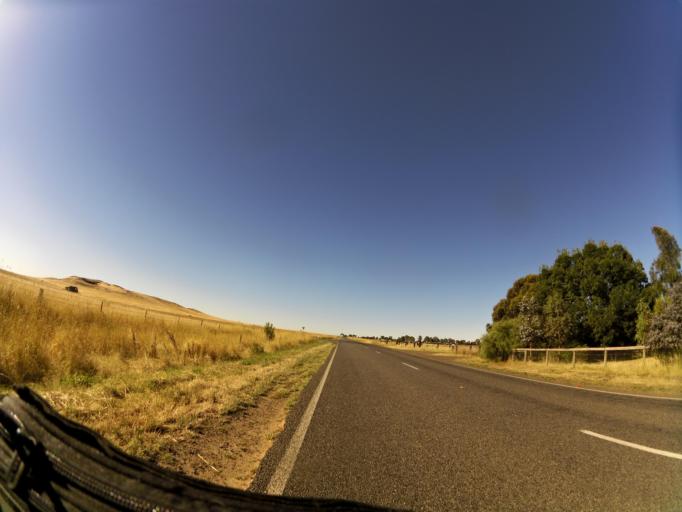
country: AU
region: Victoria
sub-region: Ballarat North
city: Delacombe
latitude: -37.6272
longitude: 143.3457
